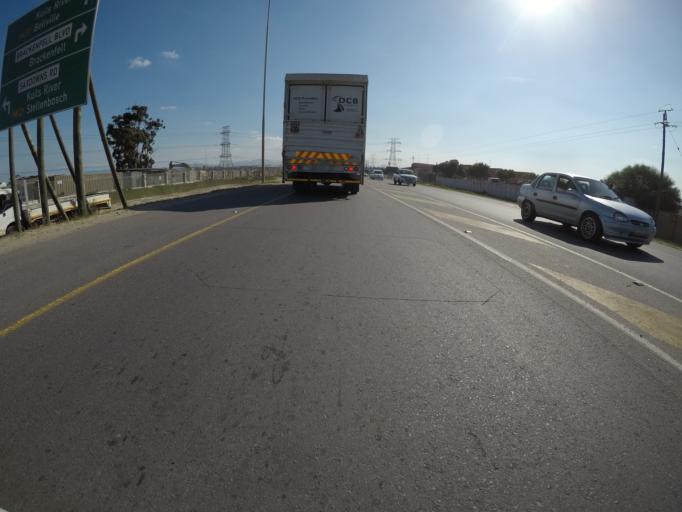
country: ZA
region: Western Cape
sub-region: City of Cape Town
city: Kraaifontein
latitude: -33.9044
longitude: 18.6984
